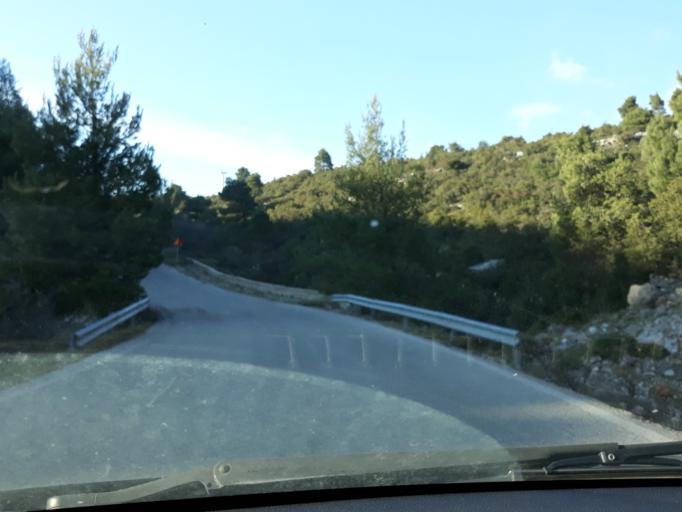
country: GR
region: Attica
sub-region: Nomarchia Dytikis Attikis
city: Fyli
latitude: 38.1565
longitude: 23.6307
